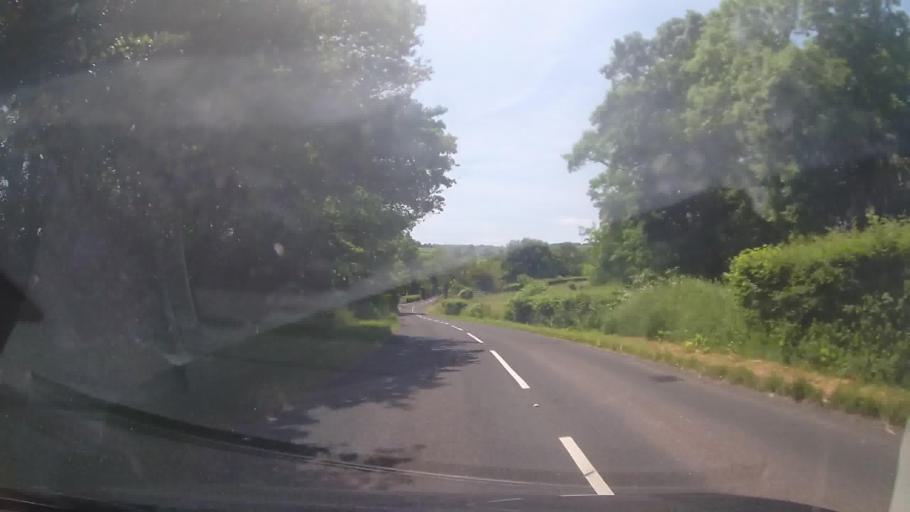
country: GB
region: England
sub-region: Herefordshire
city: Llanrothal
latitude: 51.8927
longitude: -2.7325
